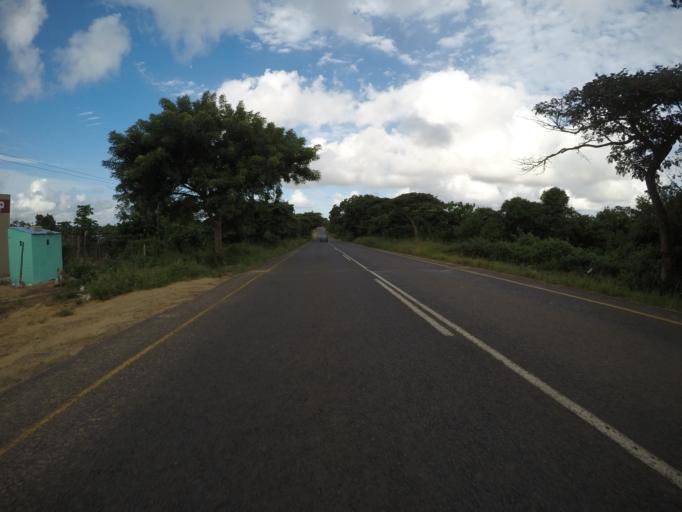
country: ZA
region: KwaZulu-Natal
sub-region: uMkhanyakude District Municipality
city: Mtubatuba
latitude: -28.3815
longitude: 32.3595
